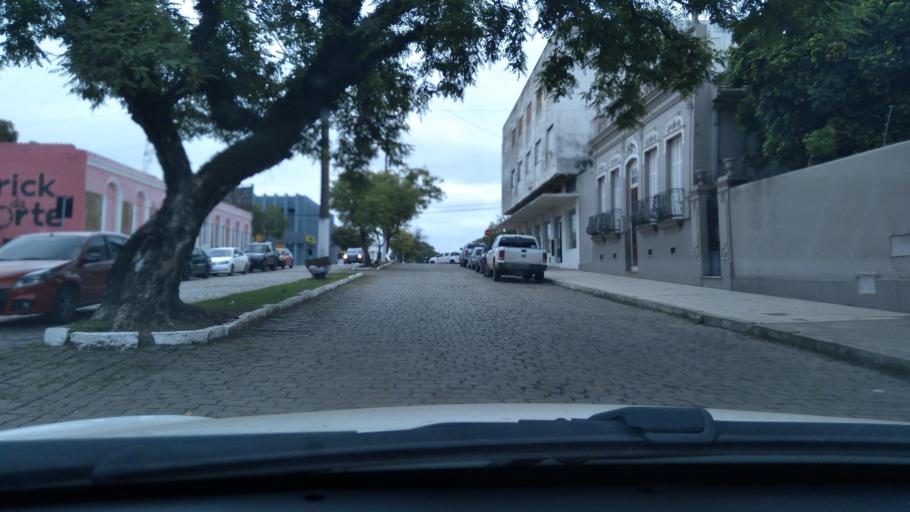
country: BR
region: Rio Grande do Sul
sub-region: Dom Pedrito
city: Dom Pedrito
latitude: -30.9849
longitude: -54.6733
